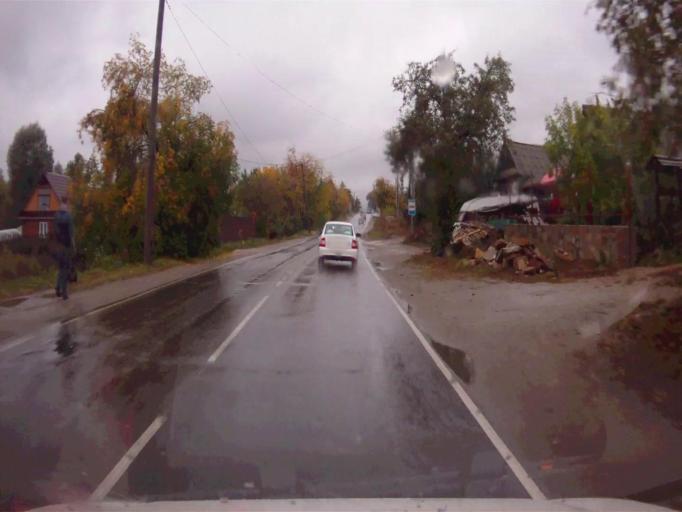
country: RU
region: Chelyabinsk
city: Kyshtym
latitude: 55.7214
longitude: 60.5361
